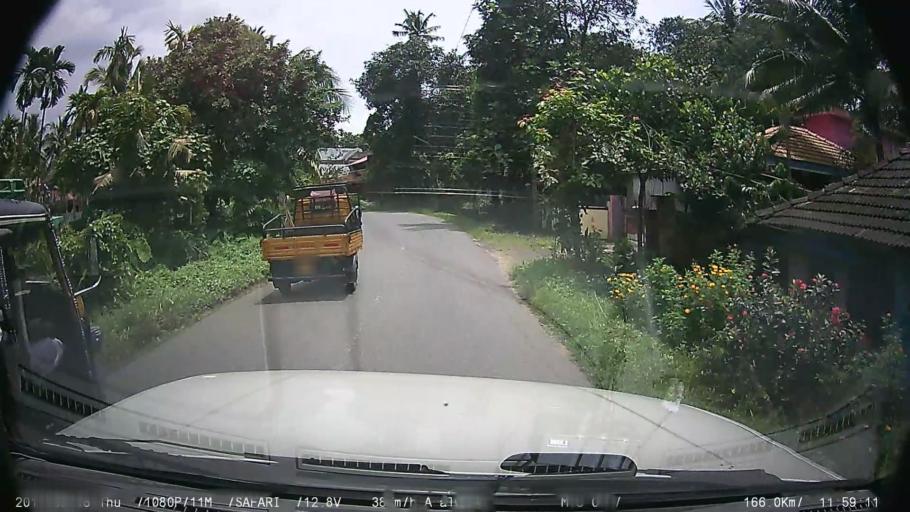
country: IN
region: Kerala
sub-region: Ernakulam
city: Kotamangalam
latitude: 10.0998
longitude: 76.6548
